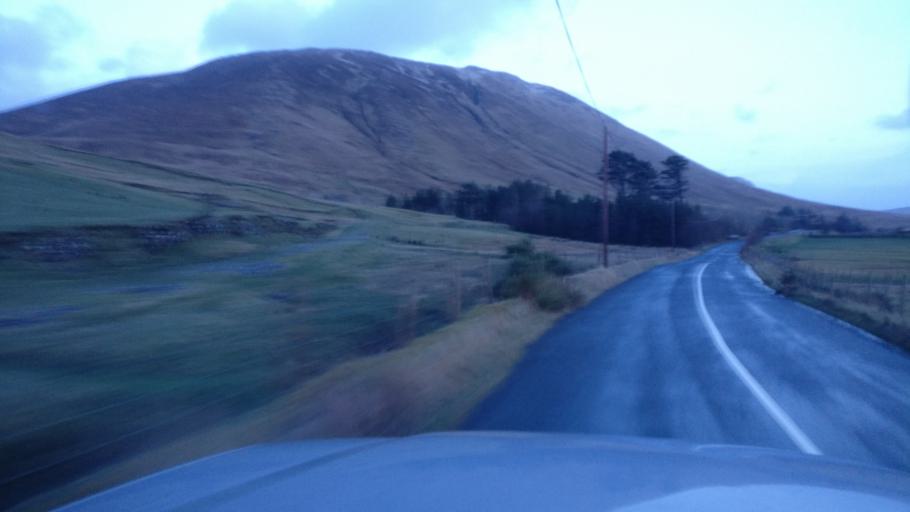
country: IE
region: Connaught
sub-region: Maigh Eo
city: Westport
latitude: 53.5722
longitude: -9.6597
